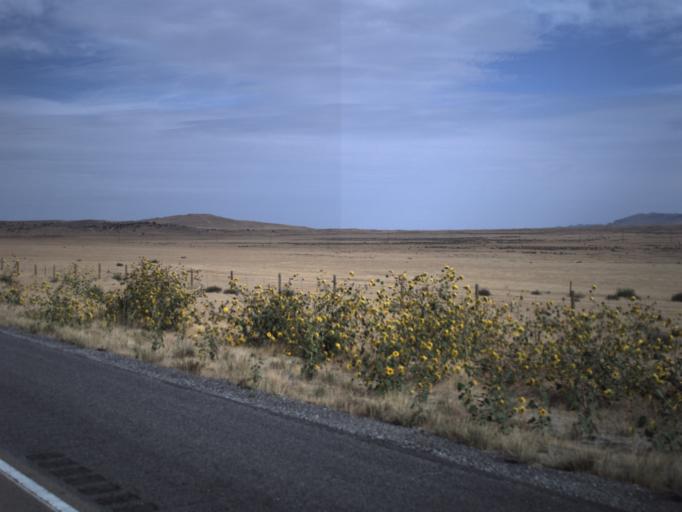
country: US
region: Utah
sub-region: Tooele County
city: Grantsville
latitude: 40.8127
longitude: -112.8723
